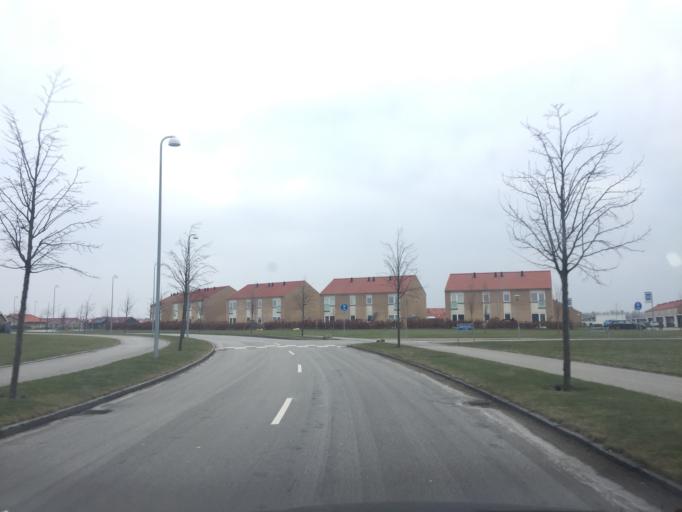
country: DK
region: Zealand
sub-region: Greve Kommune
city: Greve
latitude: 55.5971
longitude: 12.2619
